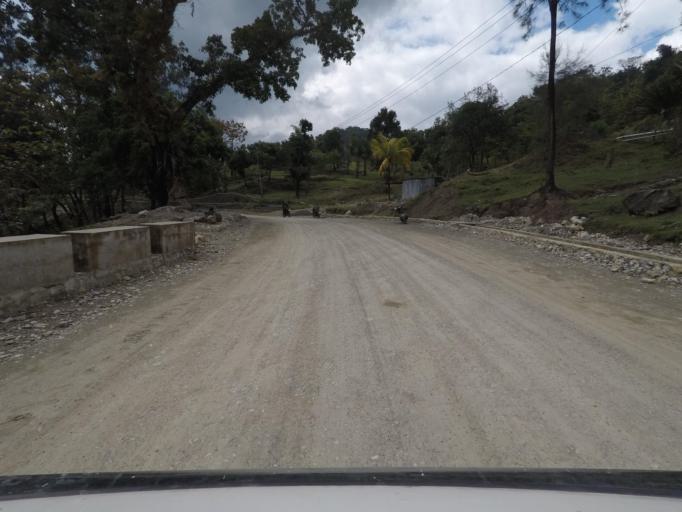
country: TL
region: Viqueque
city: Viqueque
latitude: -8.7902
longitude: 126.3763
